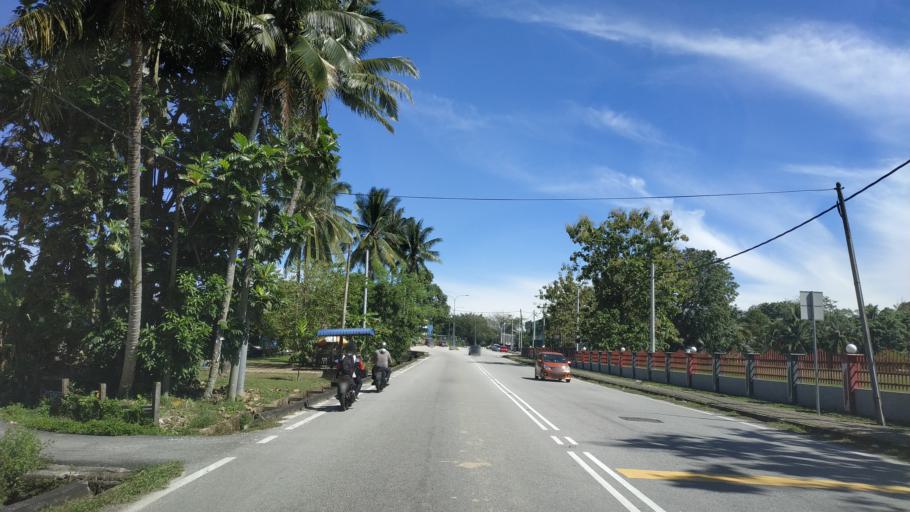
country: MY
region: Kedah
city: Kulim
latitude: 5.3529
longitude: 100.5371
